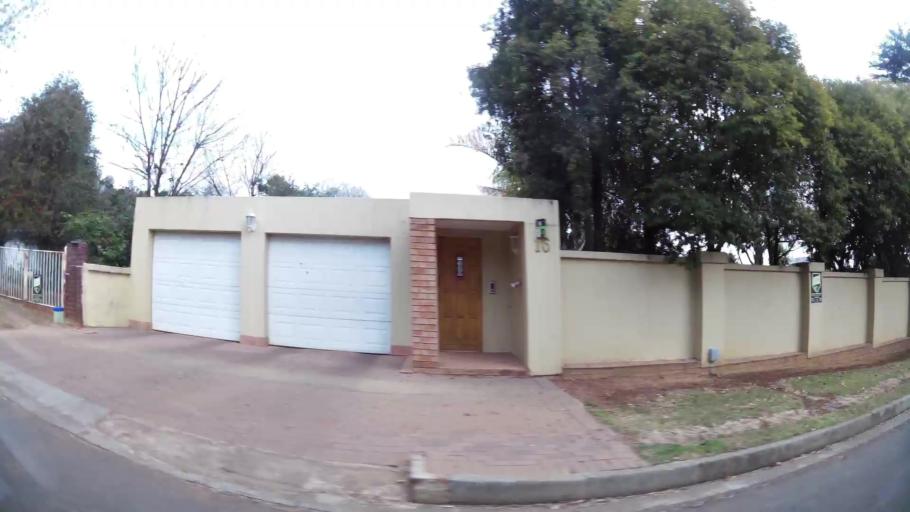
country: ZA
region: Gauteng
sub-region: City of Johannesburg Metropolitan Municipality
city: Modderfontein
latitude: -26.1391
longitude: 28.1876
